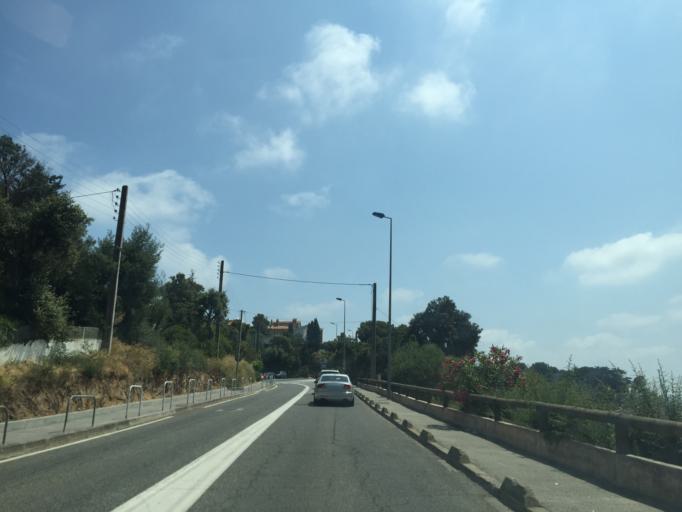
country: FR
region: Provence-Alpes-Cote d'Azur
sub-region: Departement du Var
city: Saint-Raphael
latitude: 43.4294
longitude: 6.8712
